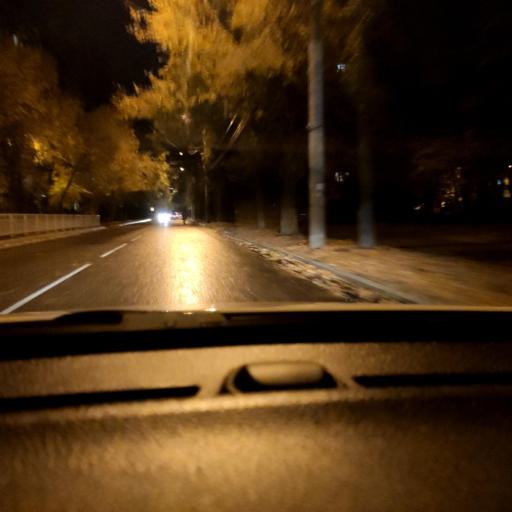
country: RU
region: Voronezj
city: Voronezh
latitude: 51.6909
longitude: 39.2611
